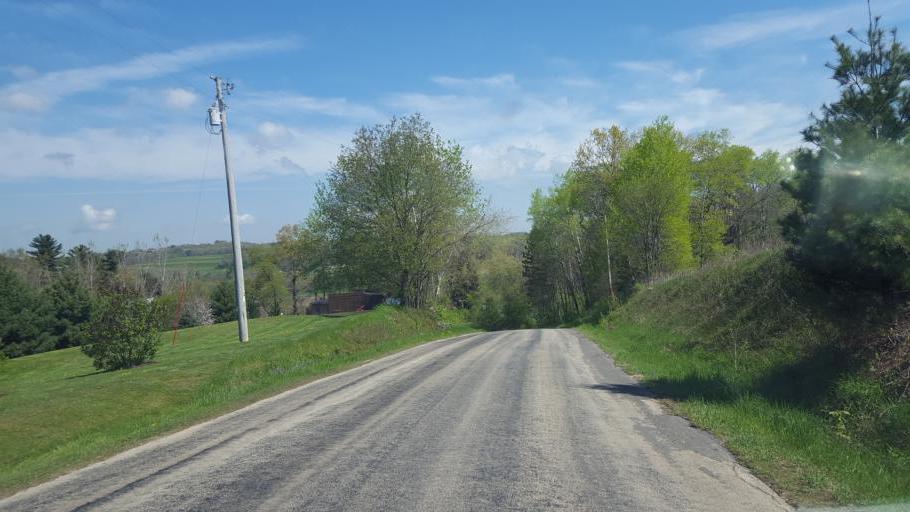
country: US
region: Wisconsin
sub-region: Juneau County
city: Elroy
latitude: 43.6967
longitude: -90.2909
